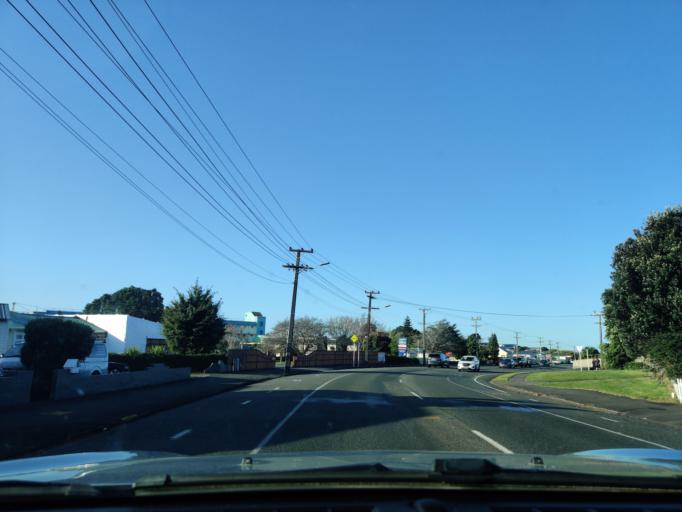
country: NZ
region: Taranaki
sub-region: New Plymouth District
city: New Plymouth
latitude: -39.0755
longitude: 174.0570
